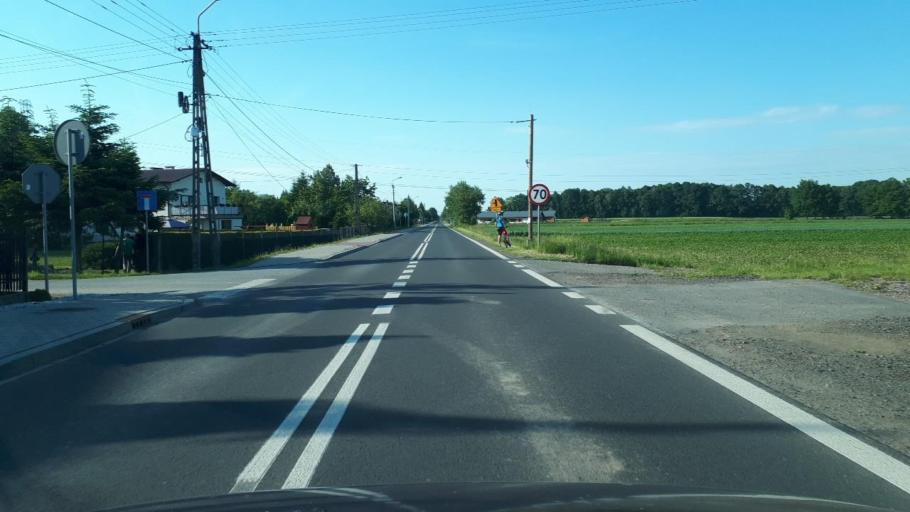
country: PL
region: Silesian Voivodeship
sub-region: Powiat bielski
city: Bronow
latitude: 49.8632
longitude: 18.9455
